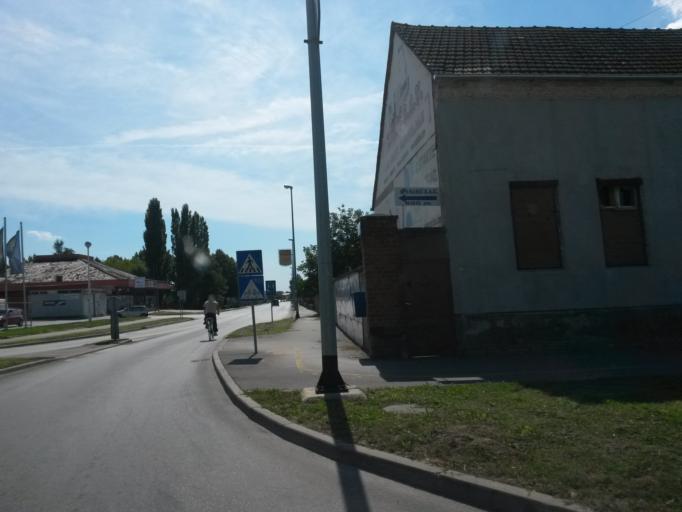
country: HR
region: Vukovarsko-Srijemska
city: Vinkovci
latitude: 45.2867
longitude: 18.8167
